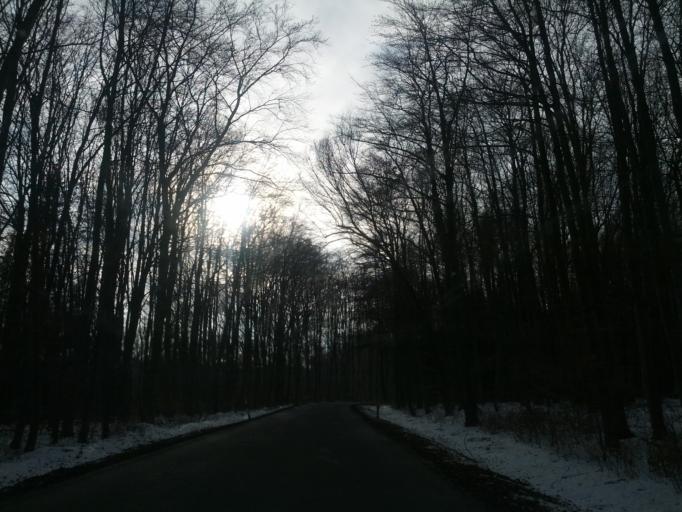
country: DE
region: Thuringia
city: Weberstedt
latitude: 51.0832
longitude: 10.5279
